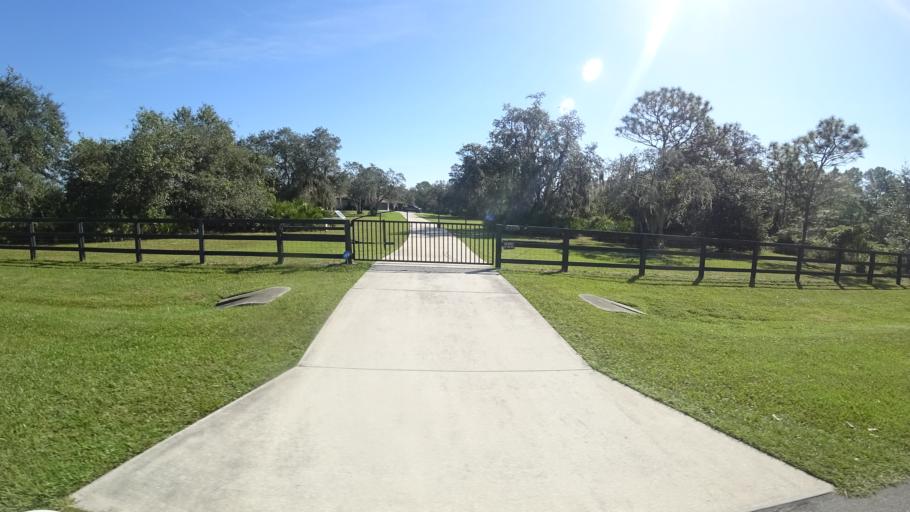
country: US
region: Florida
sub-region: Sarasota County
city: Lake Sarasota
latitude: 27.3568
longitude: -82.2507
